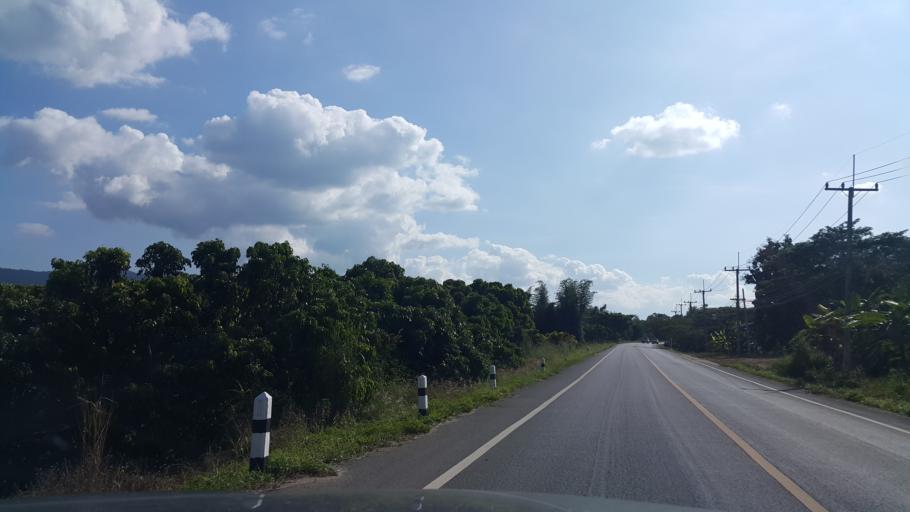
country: TH
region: Lamphun
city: Mae Tha
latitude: 18.5347
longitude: 99.2337
